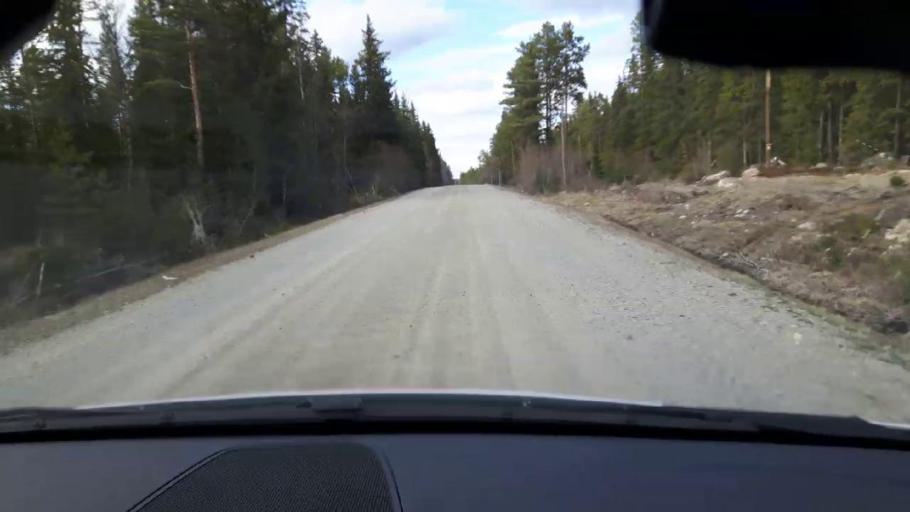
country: SE
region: Jaemtland
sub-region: Bergs Kommun
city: Hoverberg
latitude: 62.6693
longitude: 14.7461
